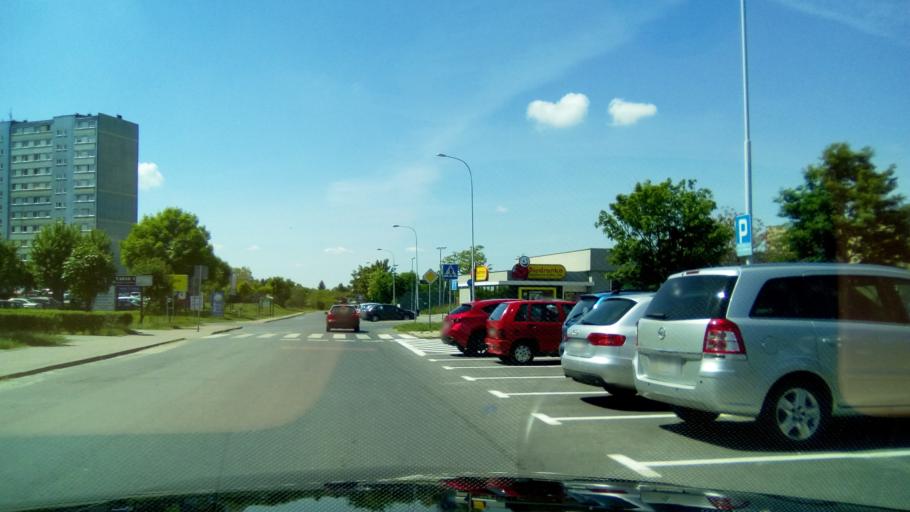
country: PL
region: Greater Poland Voivodeship
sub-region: Powiat gnieznienski
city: Gniezno
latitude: 52.5487
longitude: 17.6011
